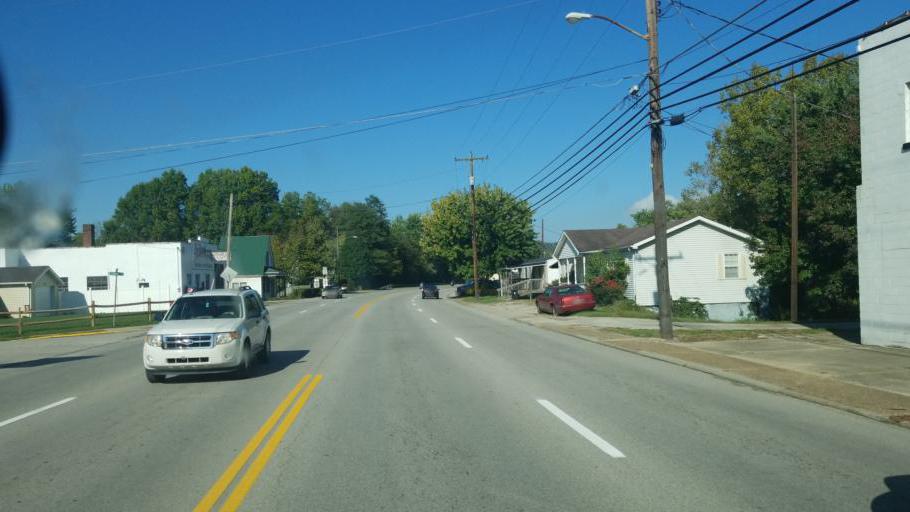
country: US
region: Ohio
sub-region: Brown County
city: Aberdeen
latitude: 38.6559
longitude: -83.7624
